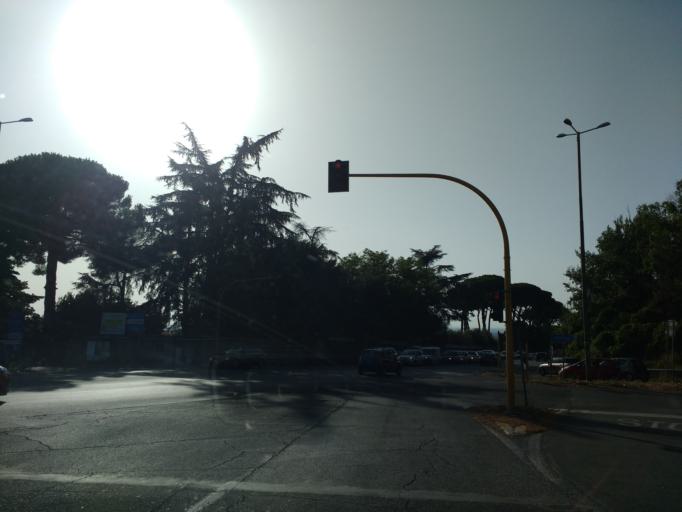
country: IT
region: Latium
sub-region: Citta metropolitana di Roma Capitale
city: Marino
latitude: 41.7556
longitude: 12.6291
